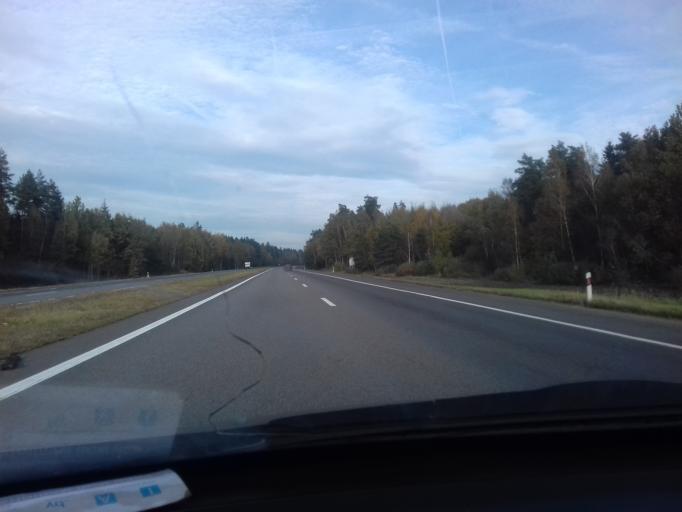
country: BY
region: Minsk
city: Hatava
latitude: 53.7480
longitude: 27.6389
